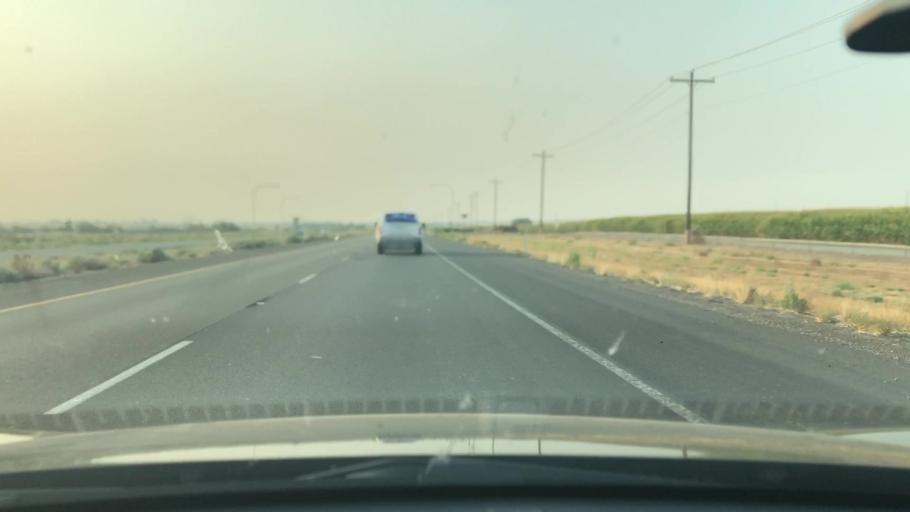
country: US
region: Washington
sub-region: Walla Walla County
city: Burbank
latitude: 46.1440
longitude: -118.9369
